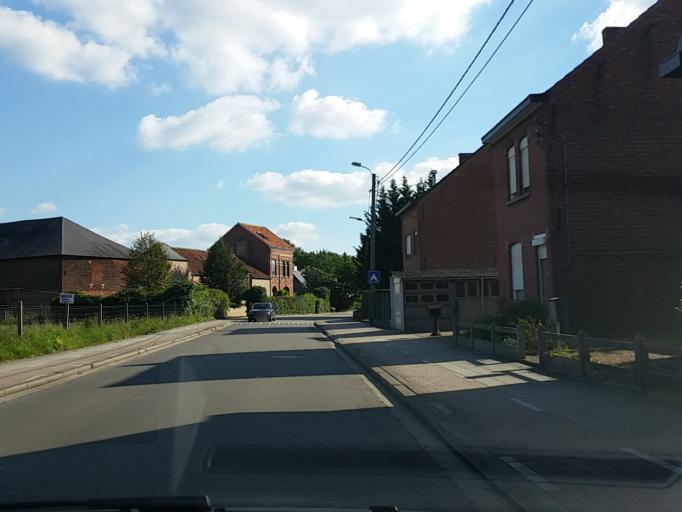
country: BE
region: Flanders
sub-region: Provincie Vlaams-Brabant
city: Rotselaar
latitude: 50.9364
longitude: 4.6965
